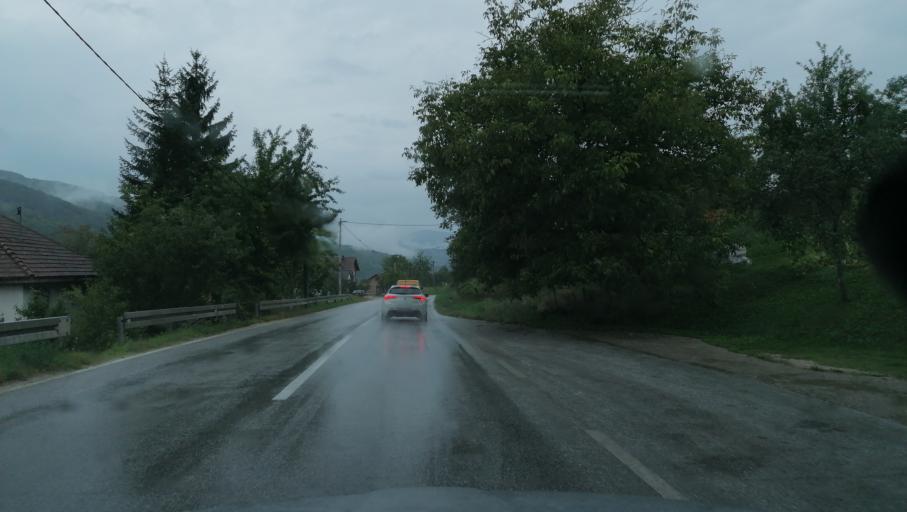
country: BA
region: Federation of Bosnia and Herzegovina
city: Gorazde
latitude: 43.6762
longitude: 19.0419
